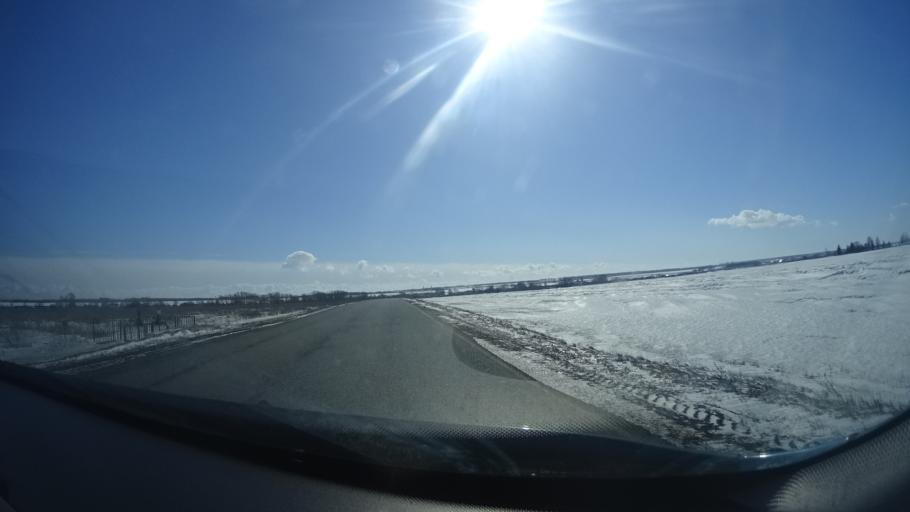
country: RU
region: Bashkortostan
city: Avdon
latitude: 54.5895
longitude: 55.8556
